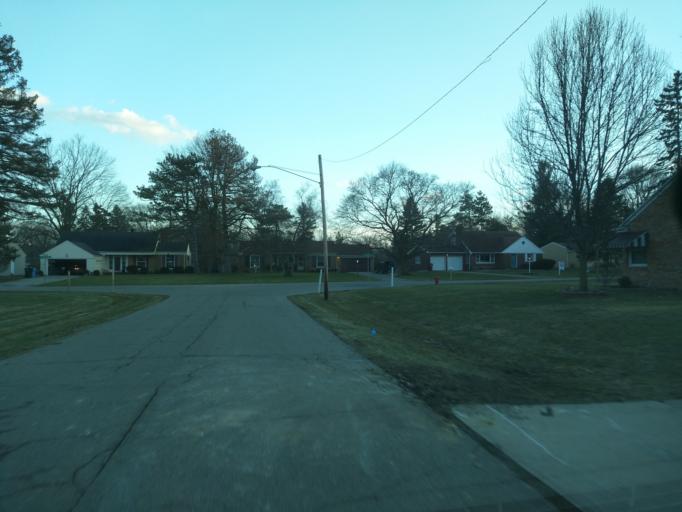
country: US
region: Michigan
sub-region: Ingham County
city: Edgemont Park
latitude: 42.7625
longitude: -84.5811
